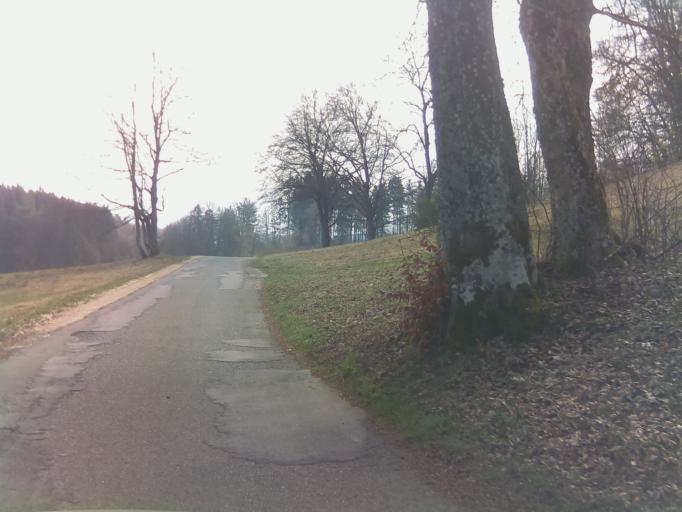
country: DE
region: Baden-Wuerttemberg
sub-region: Tuebingen Region
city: Gomadingen
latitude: 48.4321
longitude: 9.4315
